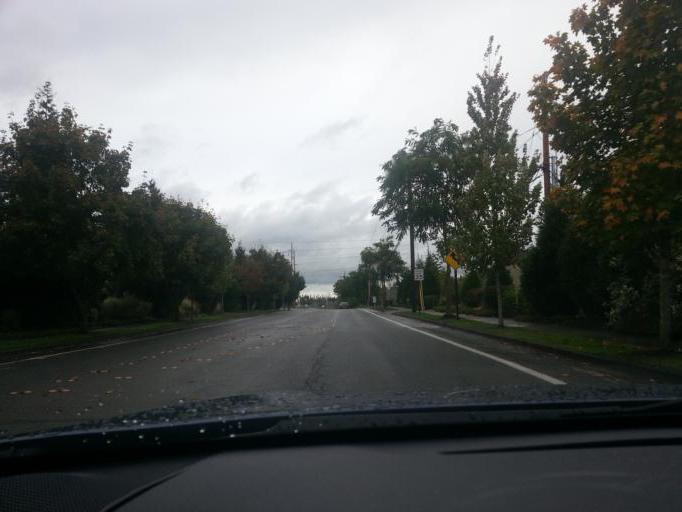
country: US
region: Washington
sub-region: Snohomish County
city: North Creek
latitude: 47.8095
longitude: -122.1807
